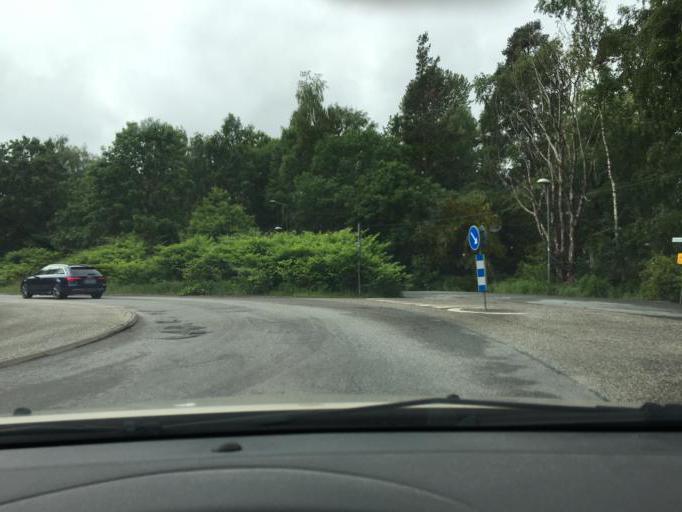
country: SE
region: Stockholm
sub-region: Varmdo Kommun
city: Hemmesta
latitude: 59.3215
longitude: 18.4816
